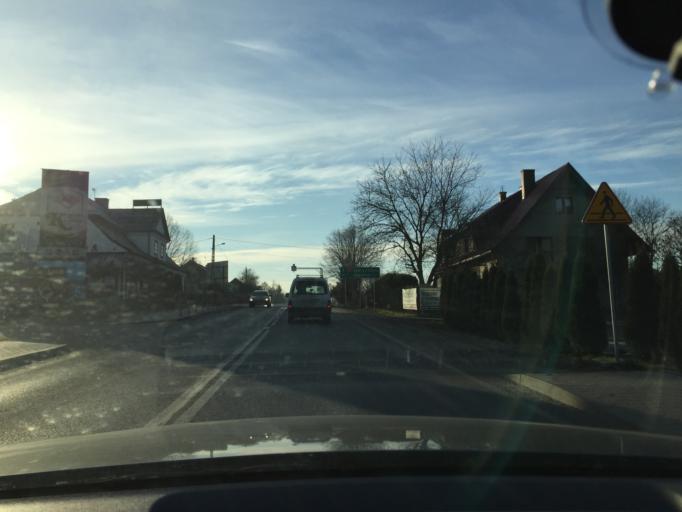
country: PL
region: Lesser Poland Voivodeship
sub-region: Powiat myslenicki
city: Krzywaczka
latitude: 49.8929
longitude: 19.8302
